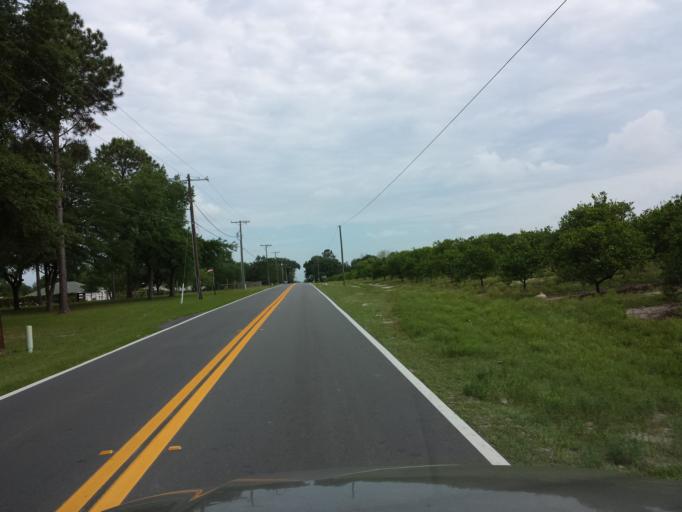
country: US
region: Florida
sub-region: Pasco County
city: San Antonio
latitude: 28.3583
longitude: -82.2744
